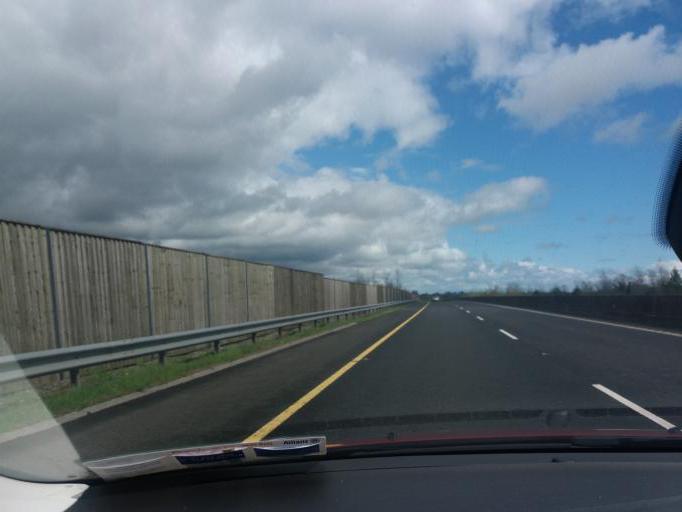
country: IE
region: Munster
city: Thurles
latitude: 52.6129
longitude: -7.7870
